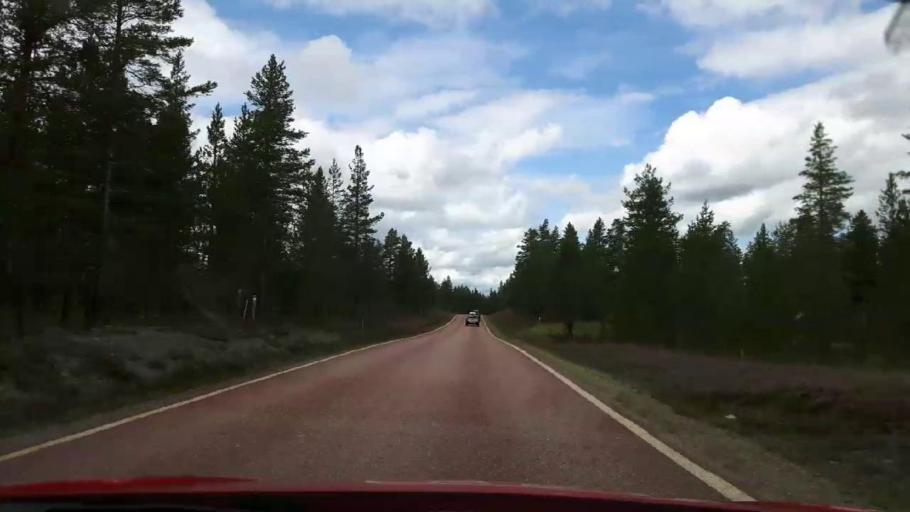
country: NO
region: Hedmark
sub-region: Trysil
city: Innbygda
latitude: 61.8543
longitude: 12.9491
